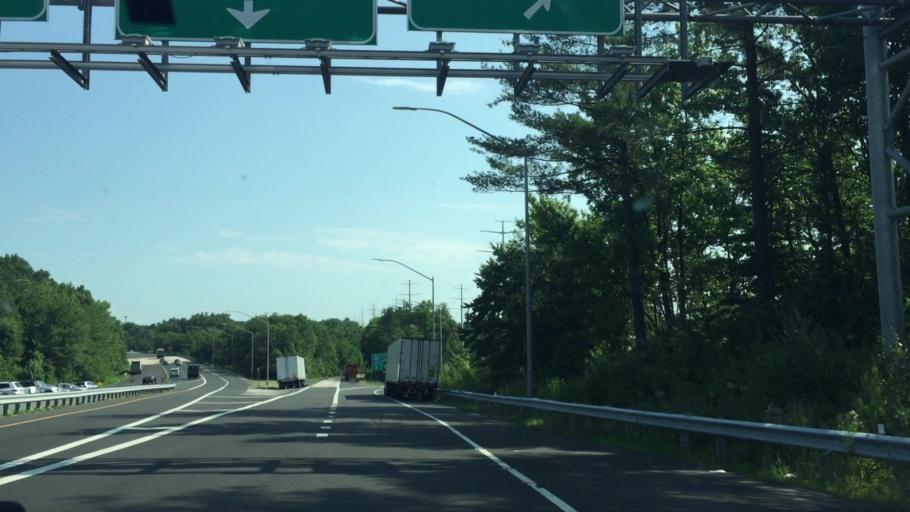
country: US
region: Maryland
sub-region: Montgomery County
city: Hillandale
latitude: 39.0170
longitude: -76.9516
